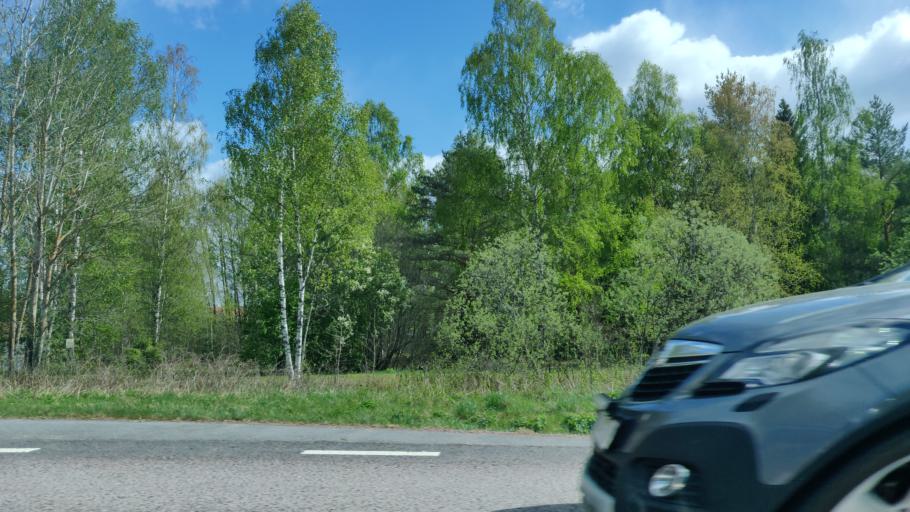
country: SE
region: Vaermland
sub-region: Karlstads Kommun
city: Skattkarr
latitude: 59.5067
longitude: 13.6145
